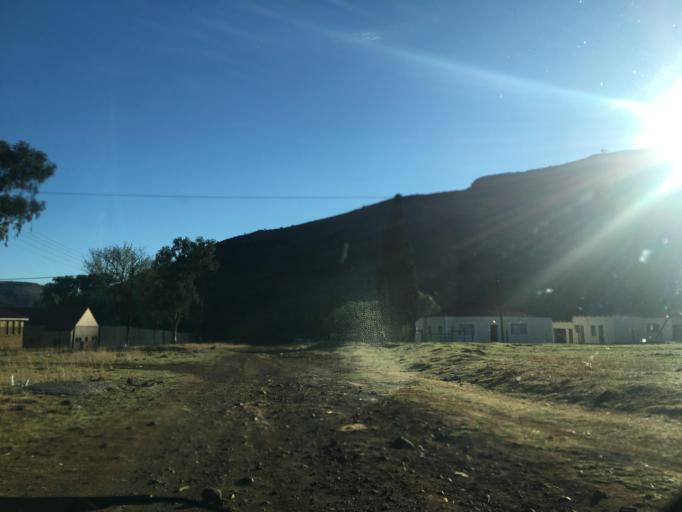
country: ZA
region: Eastern Cape
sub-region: Chris Hani District Municipality
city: Cala
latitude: -31.5269
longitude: 27.7024
